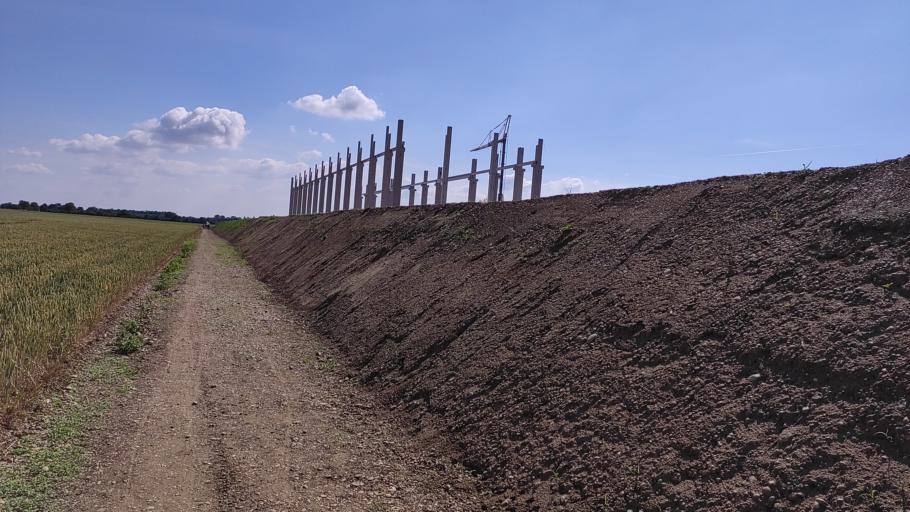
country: DE
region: Baden-Wuerttemberg
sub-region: Freiburg Region
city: Merdingen
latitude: 47.9906
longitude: 7.6552
